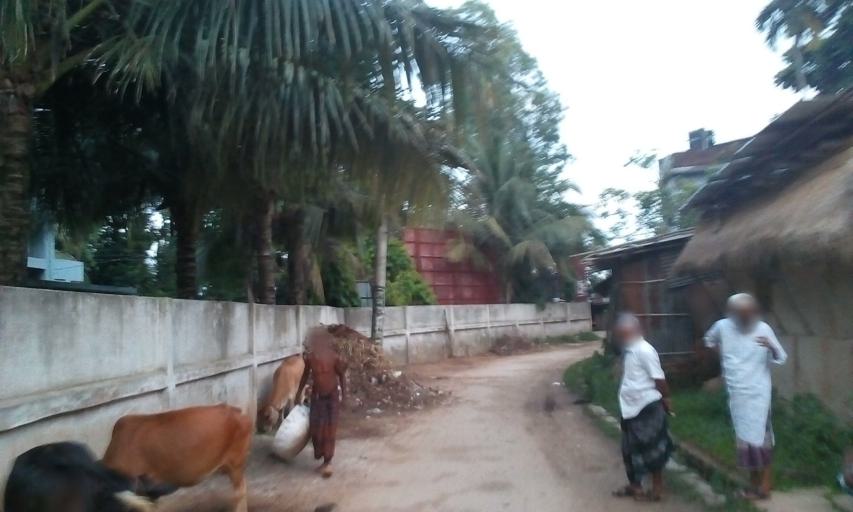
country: IN
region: West Bengal
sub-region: Dakshin Dinajpur
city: Balurghat
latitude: 25.3812
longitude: 88.9931
